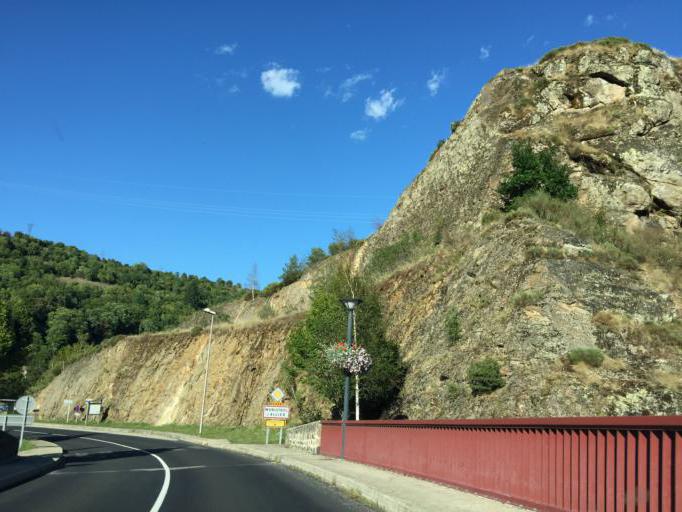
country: FR
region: Auvergne
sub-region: Departement de la Haute-Loire
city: Saugues
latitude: 44.9677
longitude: 3.6476
